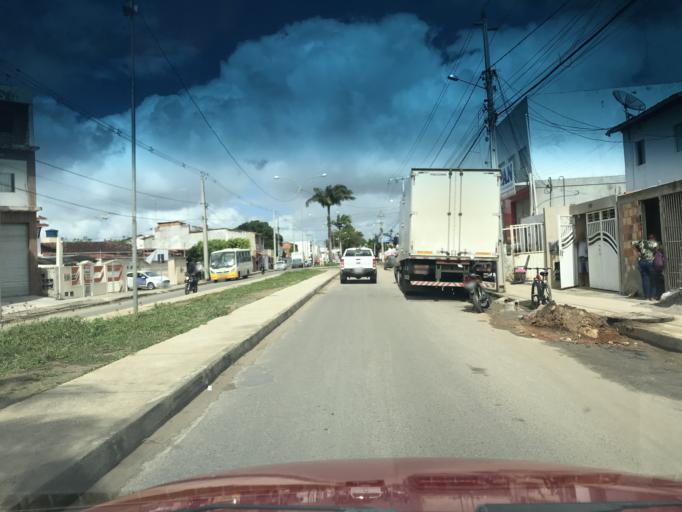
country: BR
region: Bahia
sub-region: Santo Antonio De Jesus
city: Santo Antonio de Jesus
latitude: -12.9724
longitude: -39.2728
